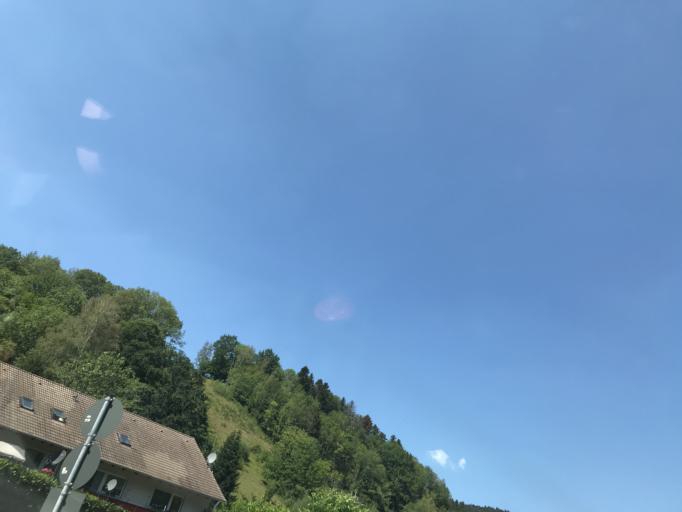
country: DE
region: Baden-Wuerttemberg
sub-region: Freiburg Region
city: Stegen
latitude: 47.9972
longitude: 7.9735
